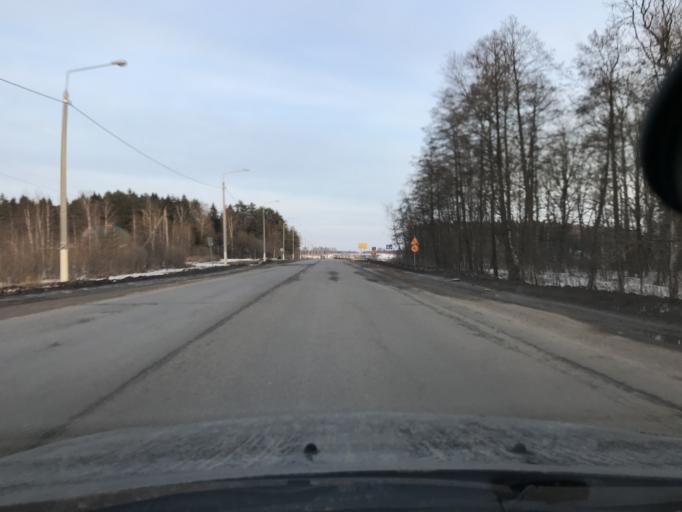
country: RU
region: Kaluga
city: Kaluga
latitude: 54.4637
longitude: 36.2598
